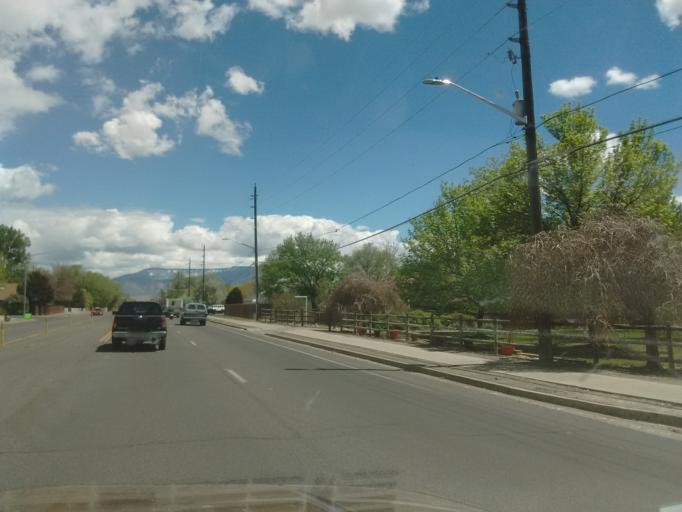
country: US
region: Colorado
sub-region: Mesa County
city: Fruitvale
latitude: 39.0917
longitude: -108.5123
